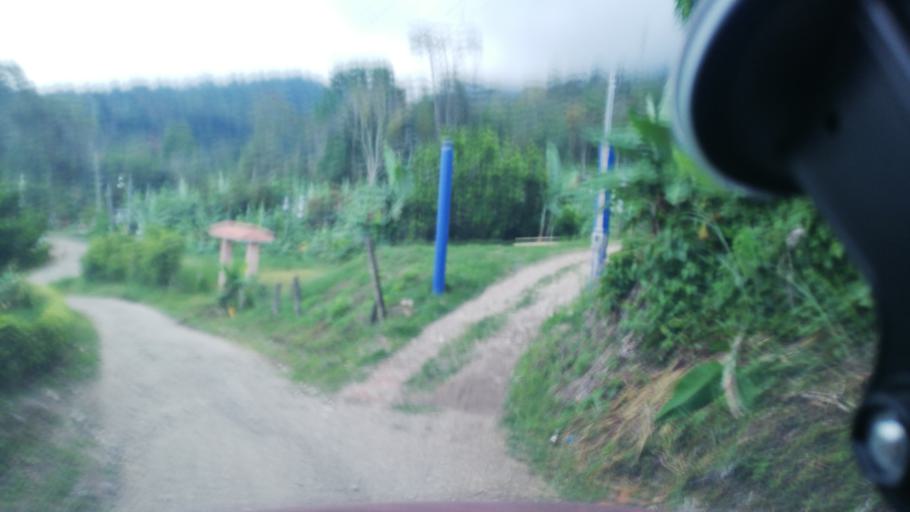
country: CO
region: Cundinamarca
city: San Antonio del Tequendama
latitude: 4.6565
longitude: -74.3933
